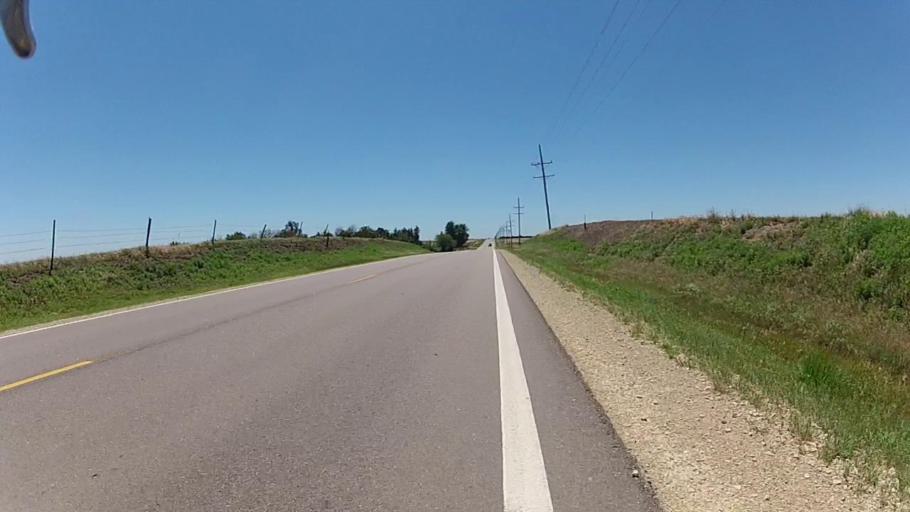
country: US
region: Kansas
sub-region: Kiowa County
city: Greensburg
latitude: 37.5429
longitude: -99.3210
